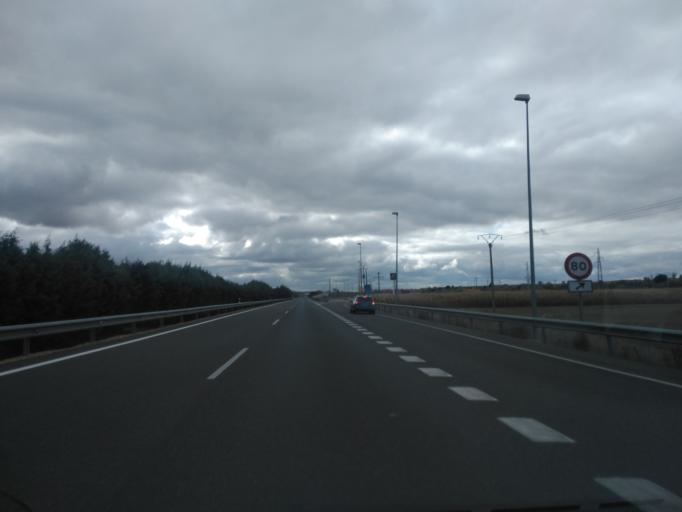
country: ES
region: Castille and Leon
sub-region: Provincia de Palencia
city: Duenas
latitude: 41.8431
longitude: -4.5631
